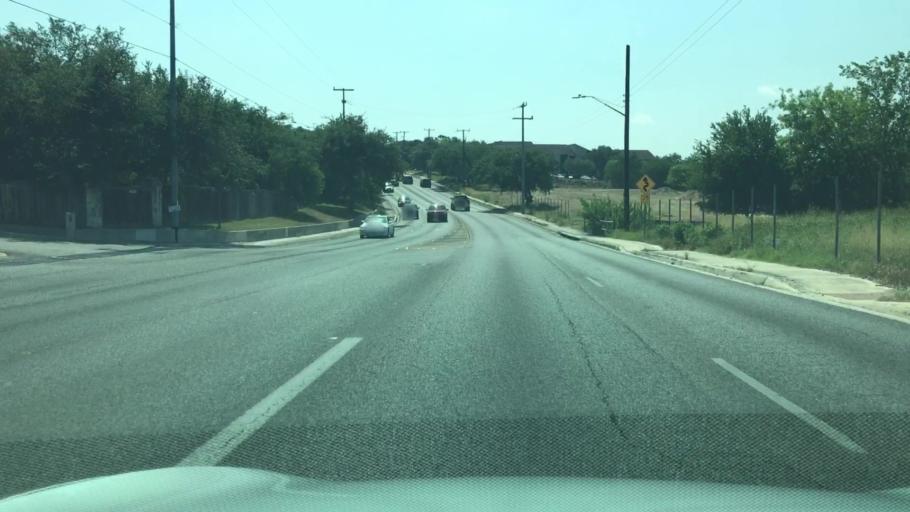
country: US
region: Texas
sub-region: Bexar County
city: Hollywood Park
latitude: 29.5902
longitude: -98.4611
